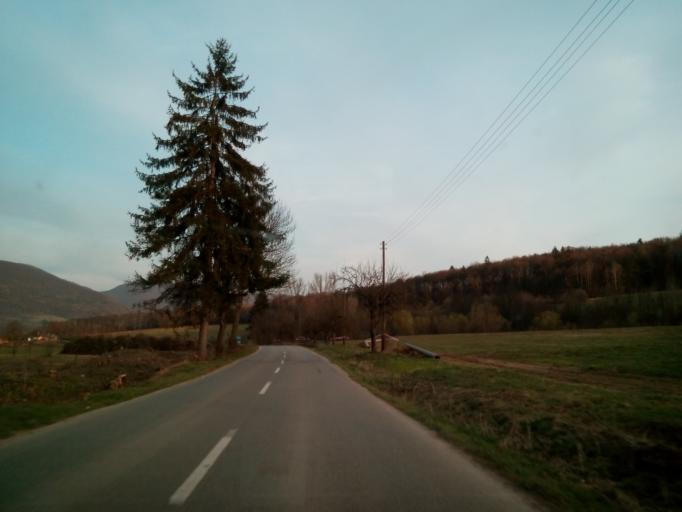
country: SK
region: Kosicky
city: Dobsina
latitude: 48.6800
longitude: 20.3359
